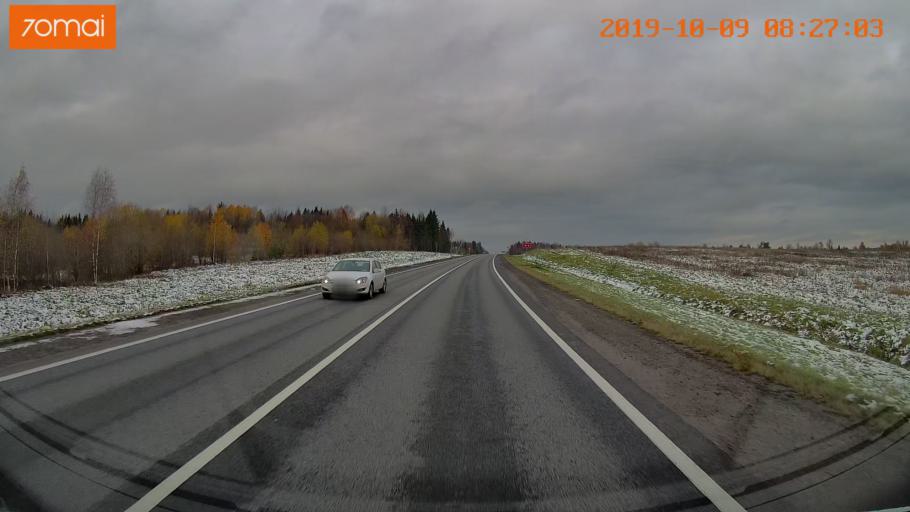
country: RU
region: Vologda
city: Gryazovets
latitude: 58.7991
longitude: 40.2554
